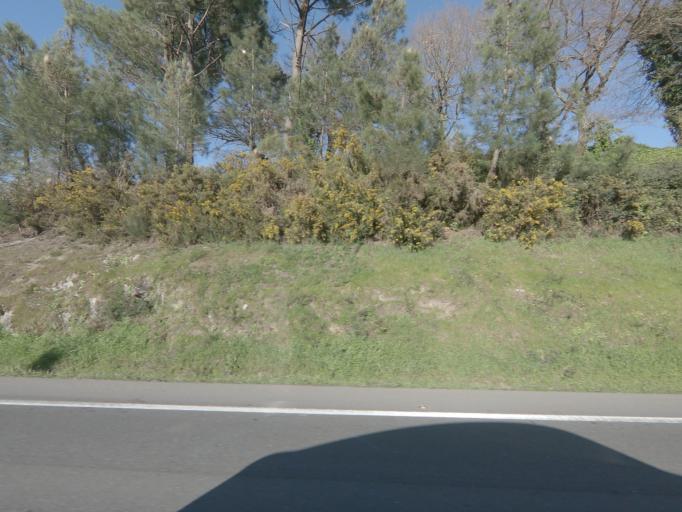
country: ES
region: Galicia
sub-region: Provincia de Pontevedra
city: Silleda
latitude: 42.7100
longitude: -8.2730
